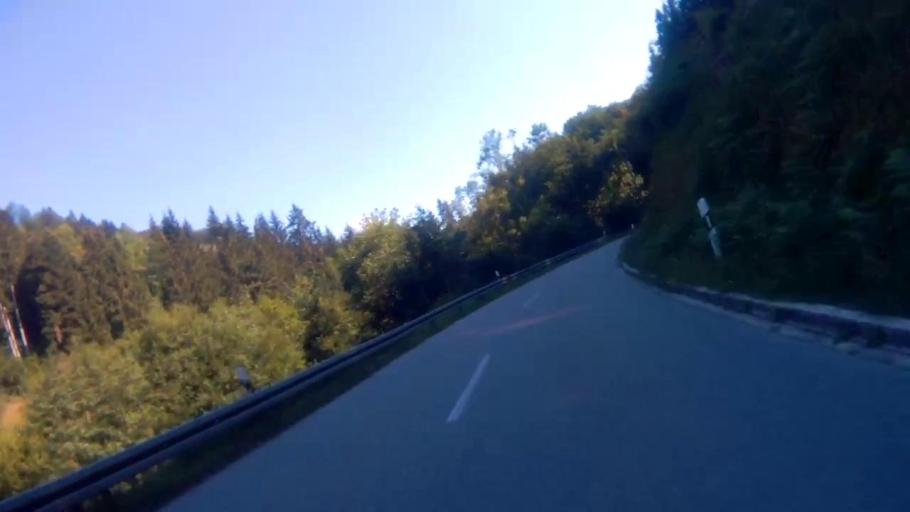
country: DE
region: Baden-Wuerttemberg
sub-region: Freiburg Region
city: Hausen
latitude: 47.6973
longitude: 7.7961
